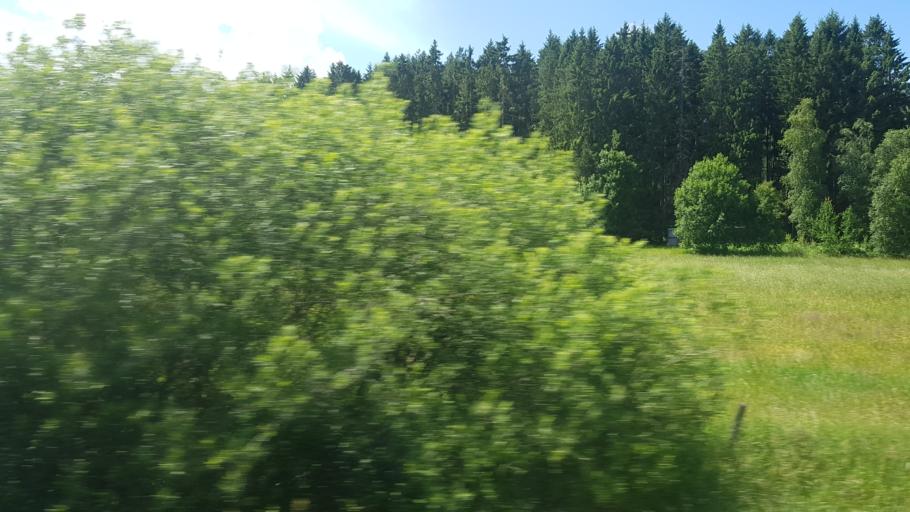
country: SE
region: Vaestra Goetaland
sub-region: Kungalvs Kommun
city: Kode
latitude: 57.9625
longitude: 11.8416
